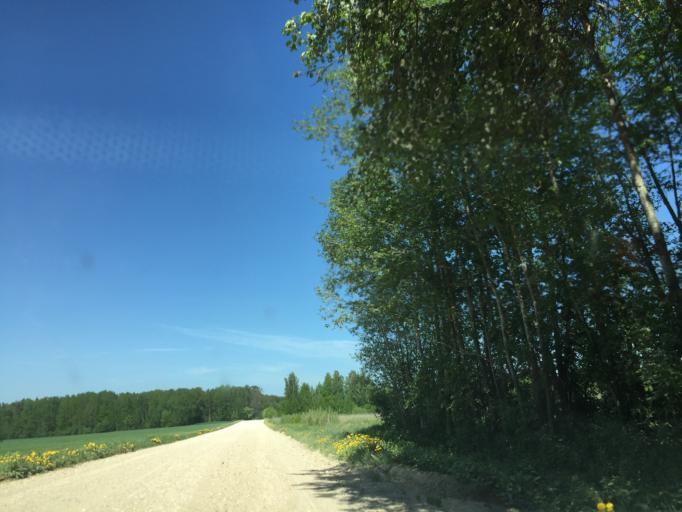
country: LV
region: Ikskile
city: Ikskile
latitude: 56.8722
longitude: 24.5002
